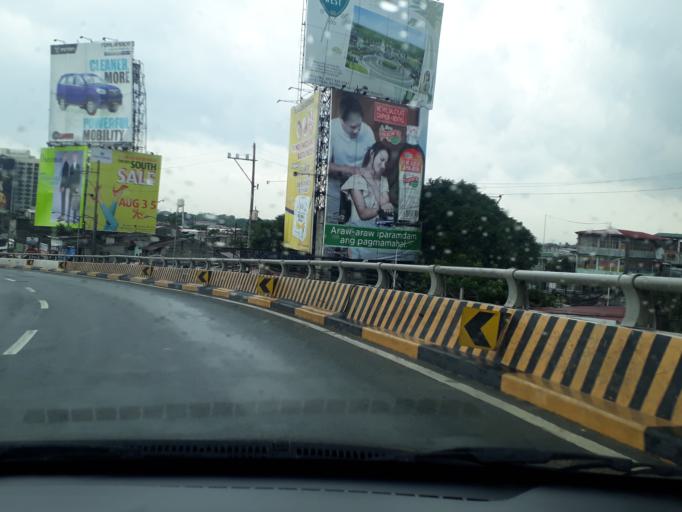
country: PH
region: Metro Manila
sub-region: Makati City
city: Makati City
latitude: 14.5111
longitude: 121.0325
